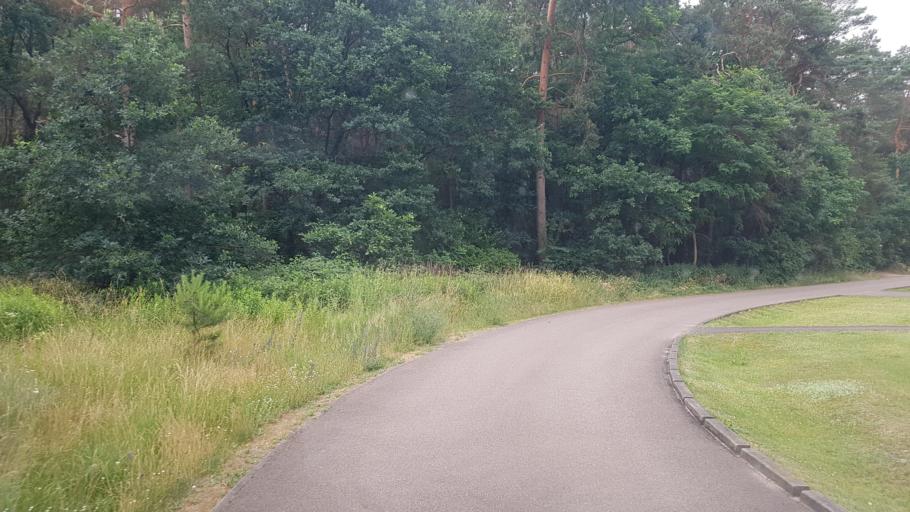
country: DE
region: Saxony-Anhalt
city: Abtsdorf
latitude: 51.8913
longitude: 12.7200
